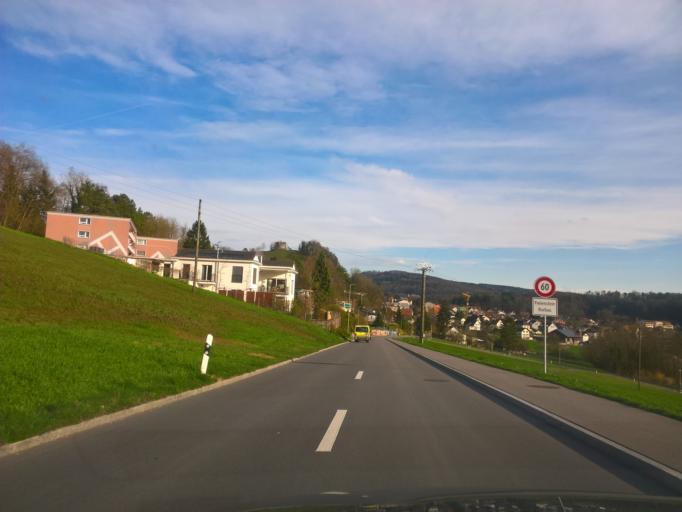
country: CH
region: Zurich
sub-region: Bezirk Buelach
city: Rorbas
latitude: 47.5373
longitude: 8.5785
